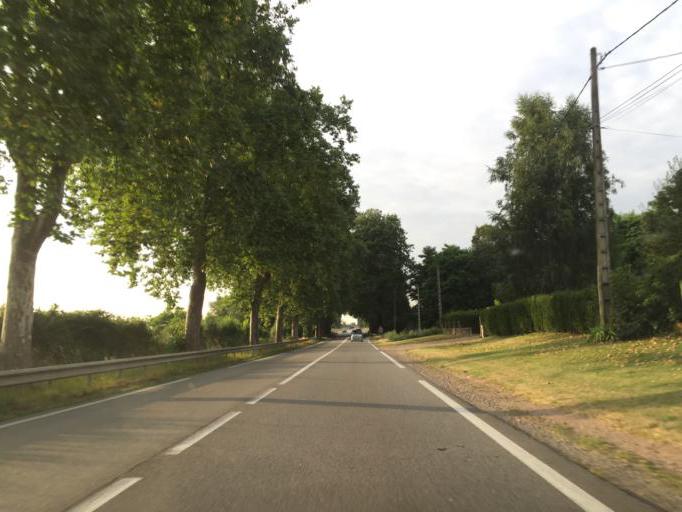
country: FR
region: Auvergne
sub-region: Departement de l'Allier
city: Varennes-sur-Allier
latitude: 46.3388
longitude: 3.3827
